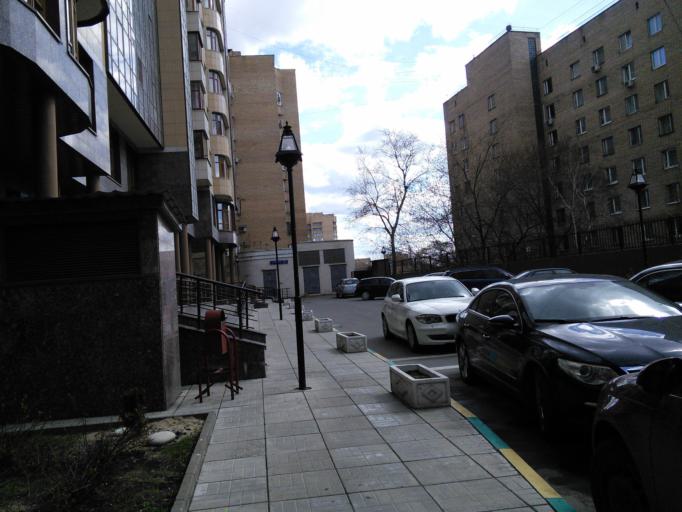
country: RU
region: Moscow
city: Taganskiy
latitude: 55.7390
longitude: 37.6524
